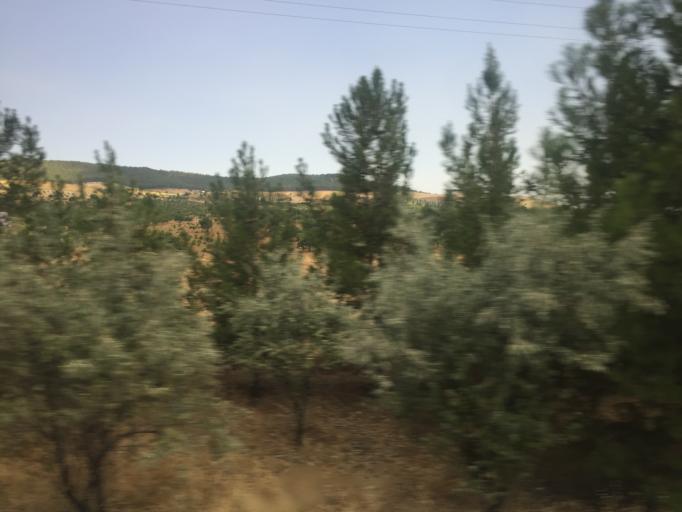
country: TR
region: Sanliurfa
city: Akziyaret
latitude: 37.2633
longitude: 38.7966
